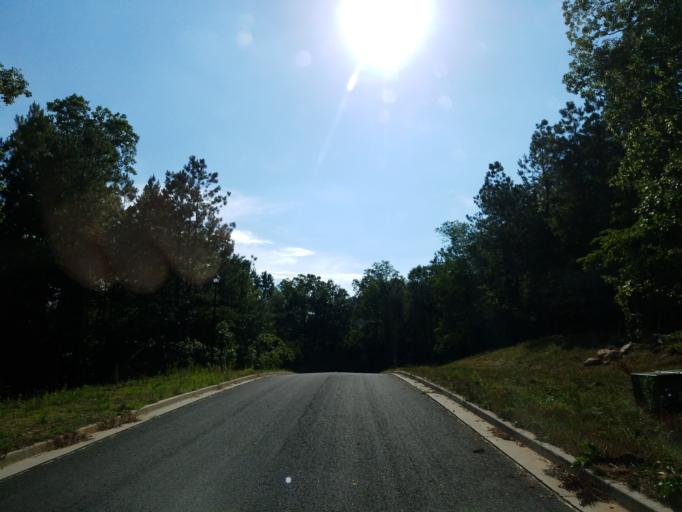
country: US
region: Georgia
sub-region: Fulton County
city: Milton
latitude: 34.1783
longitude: -84.3329
